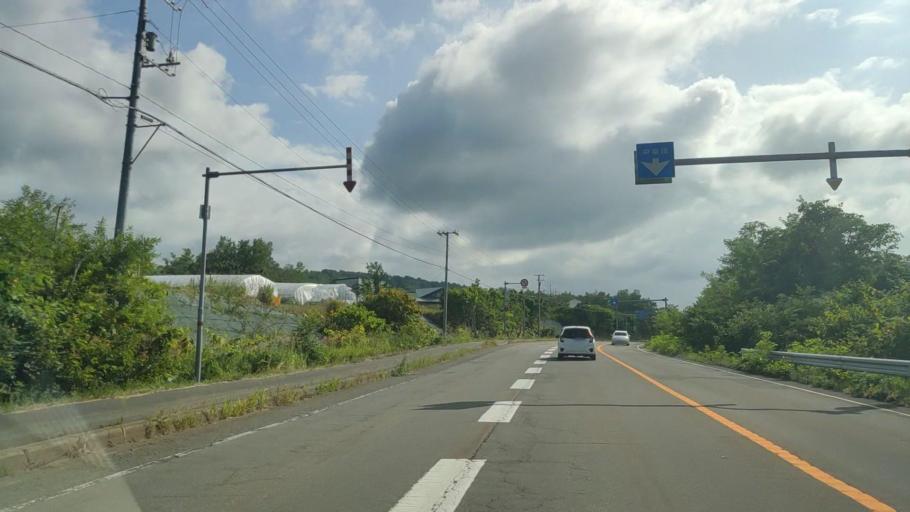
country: JP
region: Hokkaido
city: Rumoi
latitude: 43.8543
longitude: 141.5456
